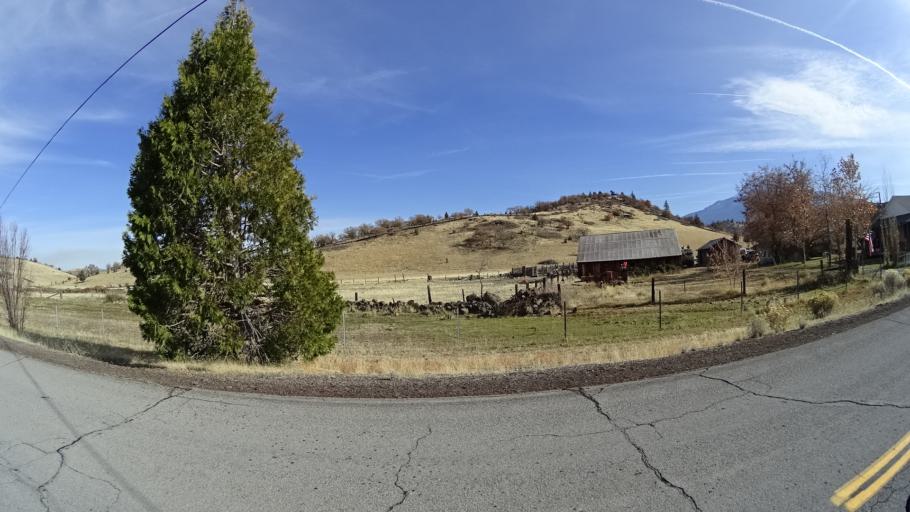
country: US
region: California
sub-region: Siskiyou County
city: Weed
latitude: 41.4693
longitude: -122.4344
